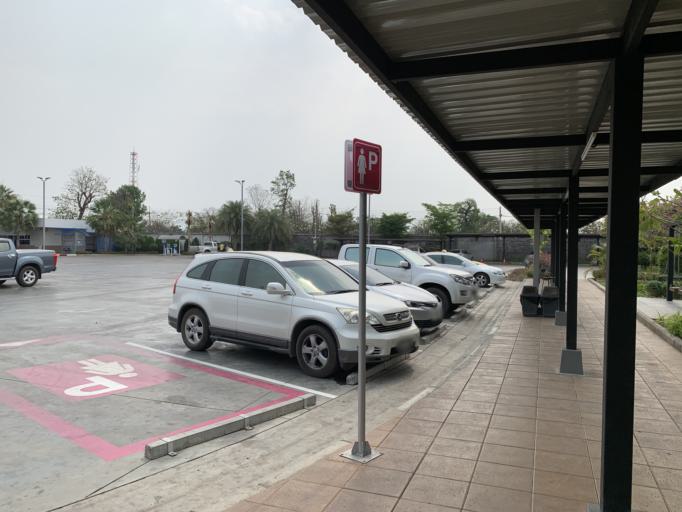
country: TH
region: Phetchabun
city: Lom Sak
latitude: 16.7570
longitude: 101.1969
